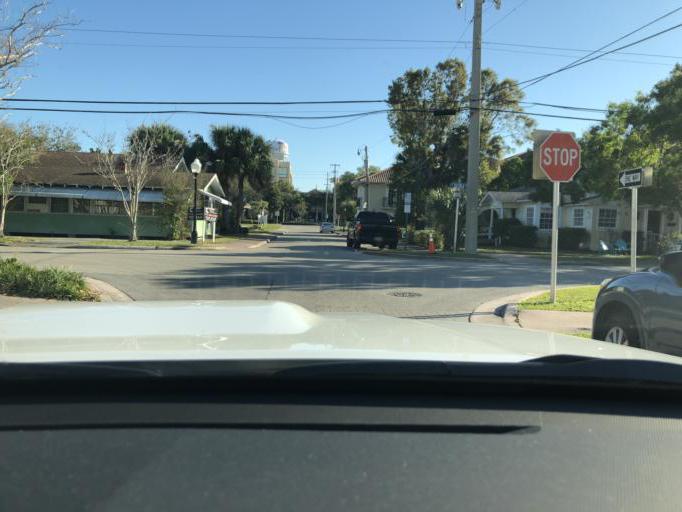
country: US
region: Florida
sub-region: Martin County
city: Stuart
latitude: 27.1986
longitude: -80.2501
